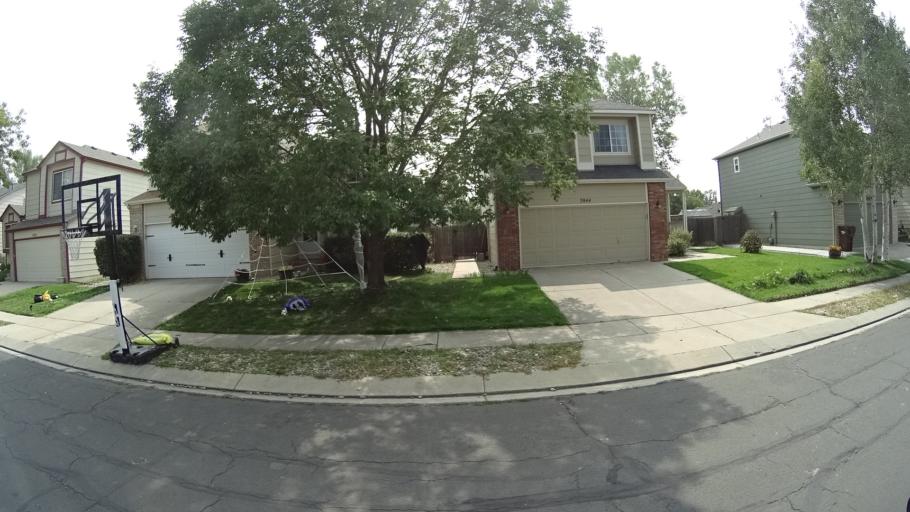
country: US
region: Colorado
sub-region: El Paso County
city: Cimarron Hills
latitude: 38.9207
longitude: -104.7271
